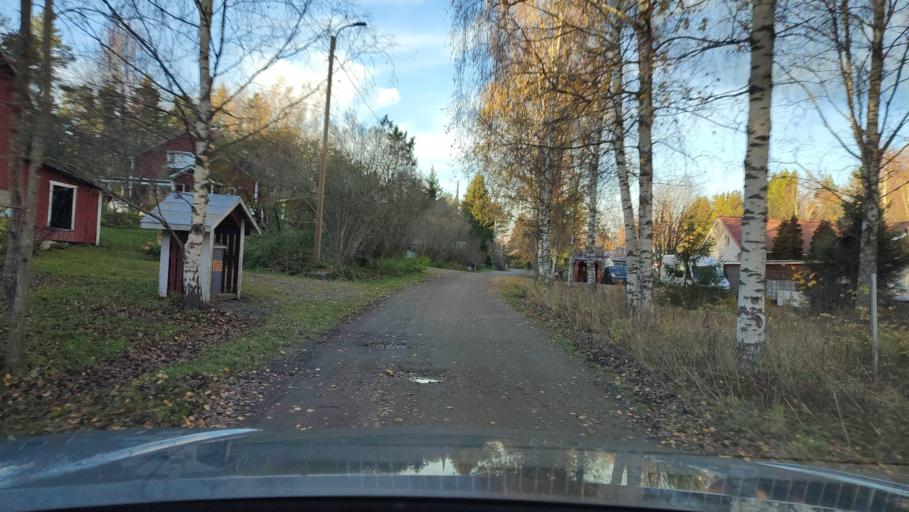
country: FI
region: Ostrobothnia
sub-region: Vaasa
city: Teeriniemi
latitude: 63.0683
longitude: 21.6953
